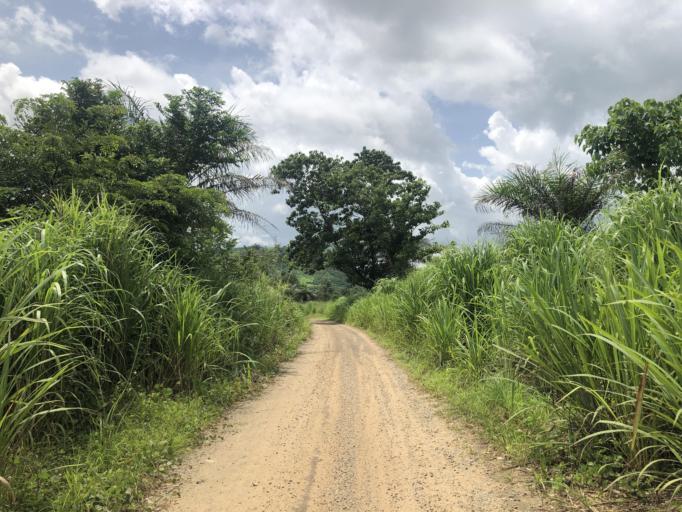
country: SL
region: Northern Province
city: Bumbuna
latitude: 9.0041
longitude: -11.7659
